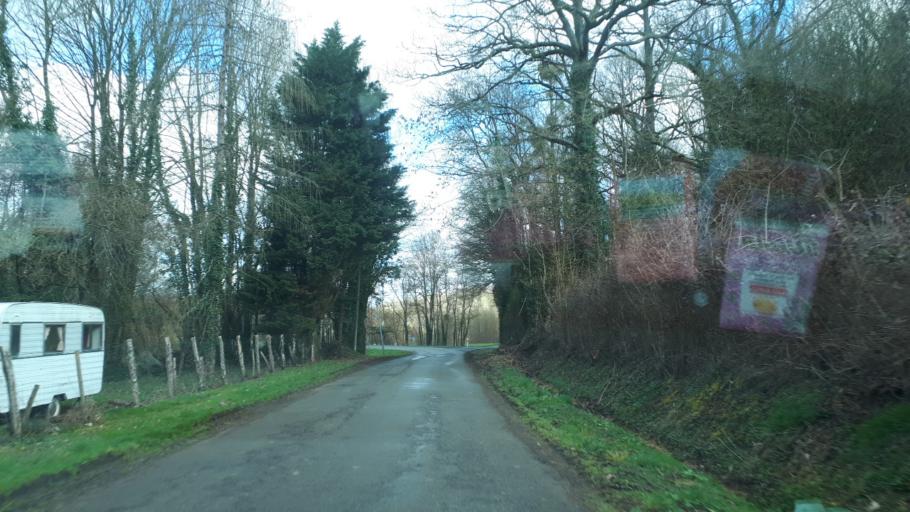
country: FR
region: Centre
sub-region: Departement du Loir-et-Cher
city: Sarge-sur-Braye
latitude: 47.9928
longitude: 0.8217
